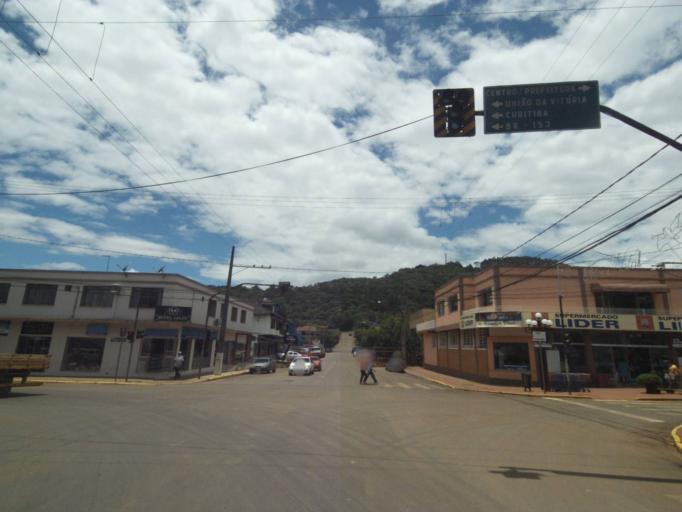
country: BR
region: Parana
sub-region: Pinhao
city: Pinhao
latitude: -26.1569
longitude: -51.5550
